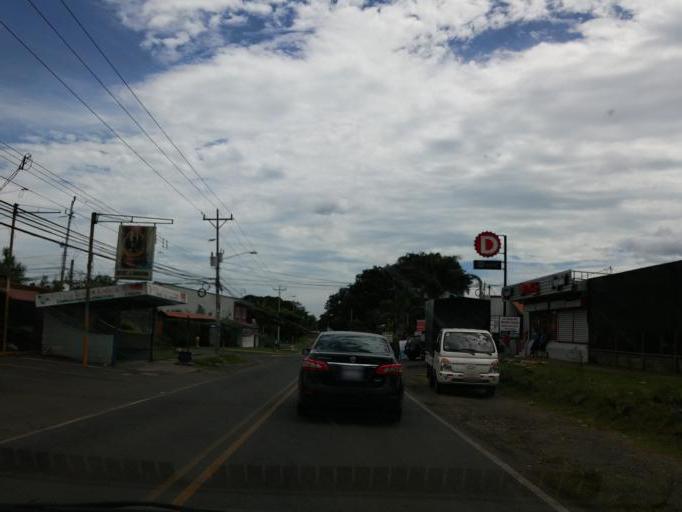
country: CR
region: Alajuela
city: Carrillos
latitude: 10.0092
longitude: -84.2613
